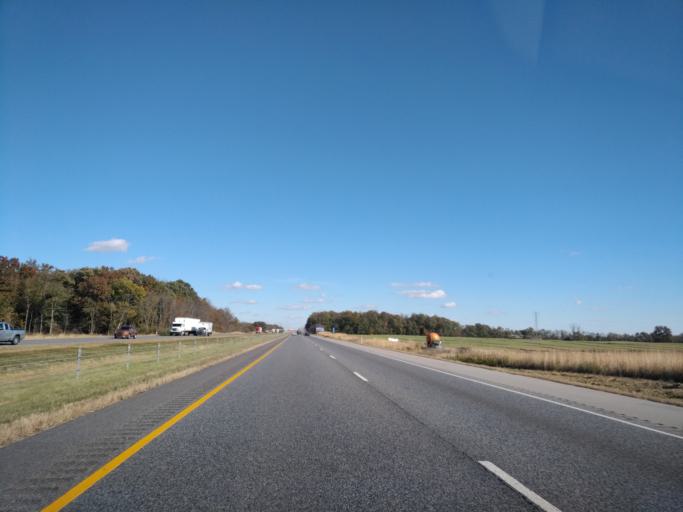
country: US
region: Indiana
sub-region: Hancock County
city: Greenfield
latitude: 39.8204
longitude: -85.8069
